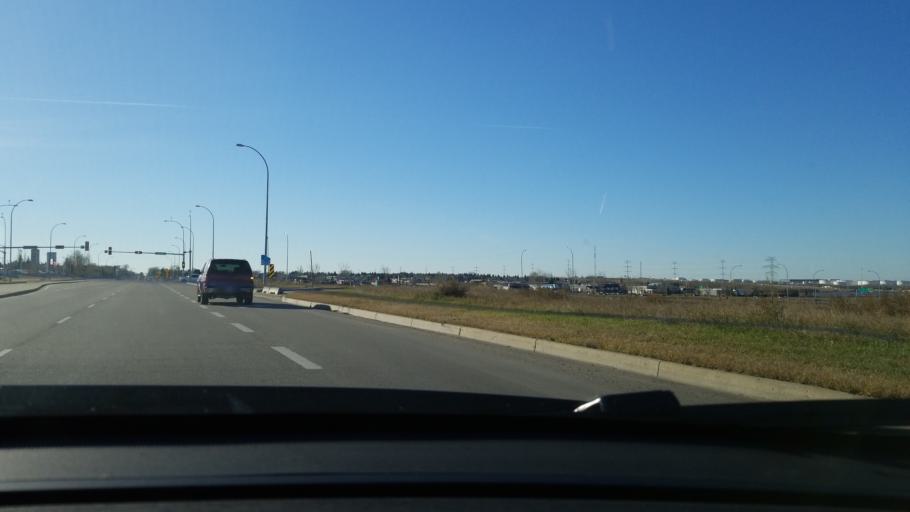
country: CA
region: Alberta
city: Sherwood Park
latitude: 53.5463
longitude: -113.3202
